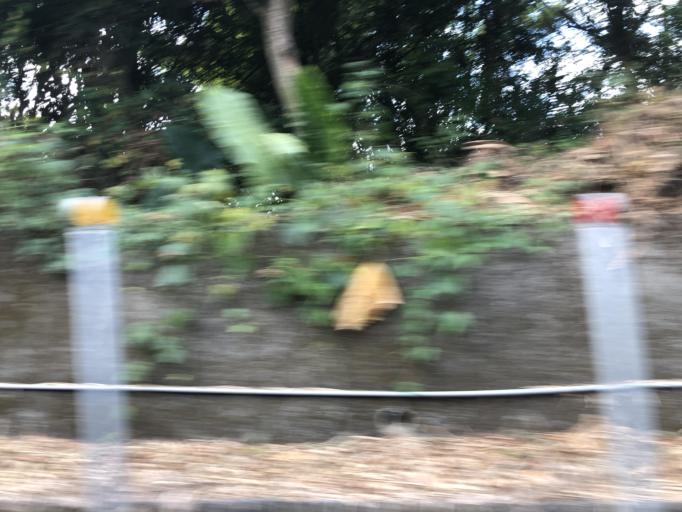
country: TW
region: Taiwan
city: Yujing
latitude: 23.0151
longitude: 120.4168
